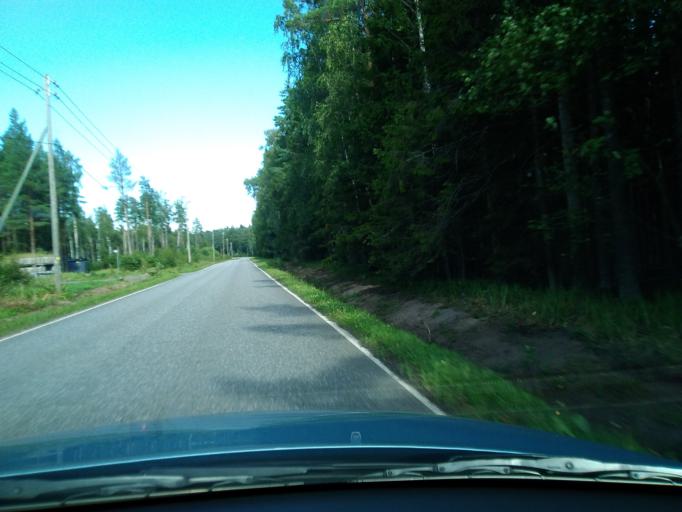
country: FI
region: Uusimaa
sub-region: Raaseporin
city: Hanko
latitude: 59.8367
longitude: 23.1543
